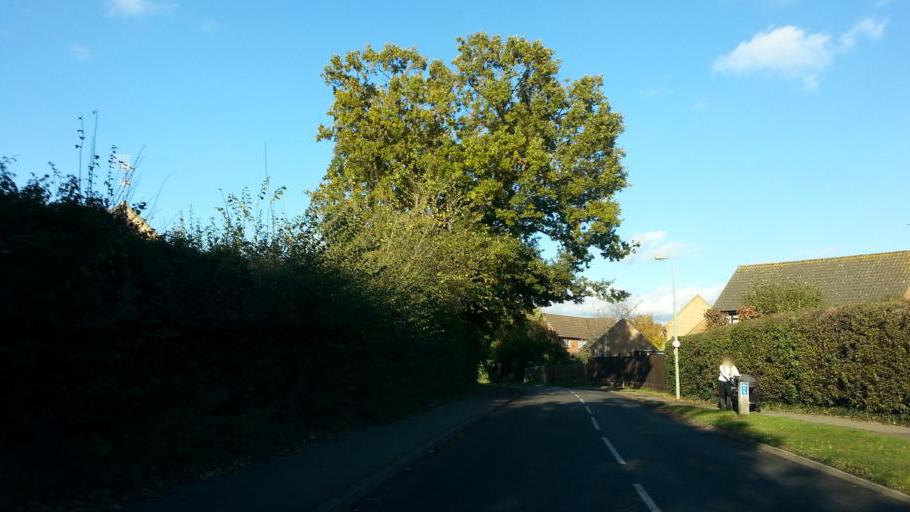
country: GB
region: England
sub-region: Suffolk
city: Thurston
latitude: 52.2529
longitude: 0.8110
